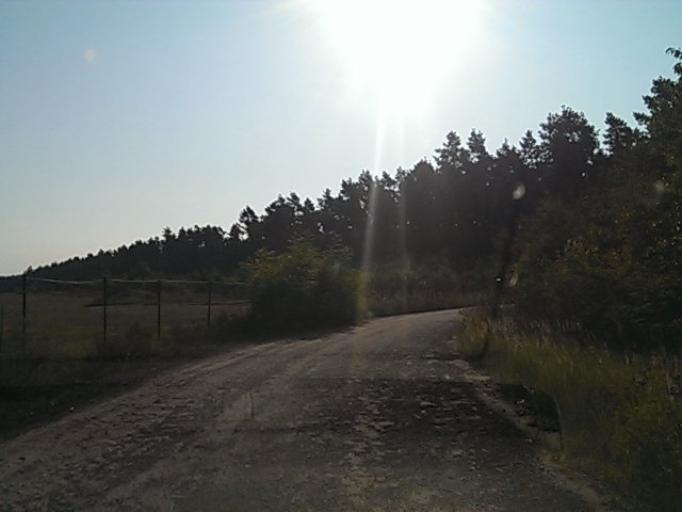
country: DE
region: Brandenburg
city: Trebbin
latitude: 52.2012
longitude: 13.1484
